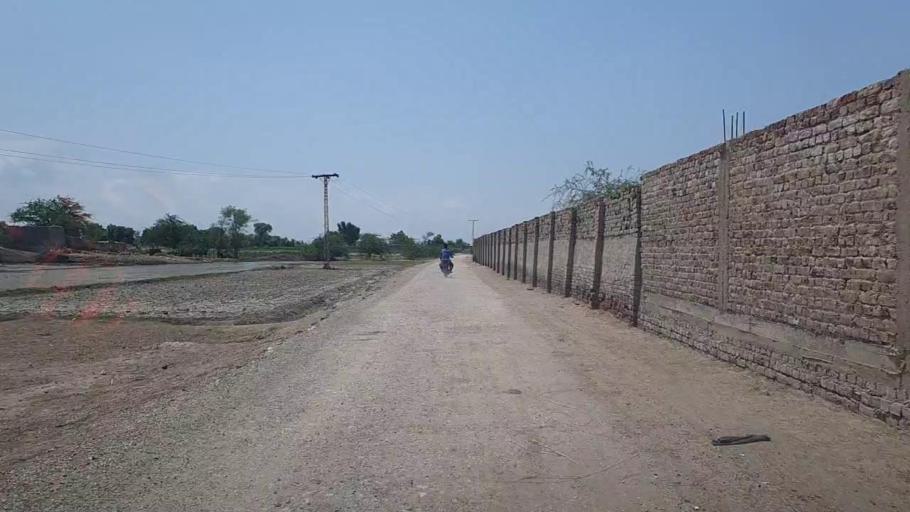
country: PK
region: Sindh
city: Ubauro
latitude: 28.1715
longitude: 69.7627
